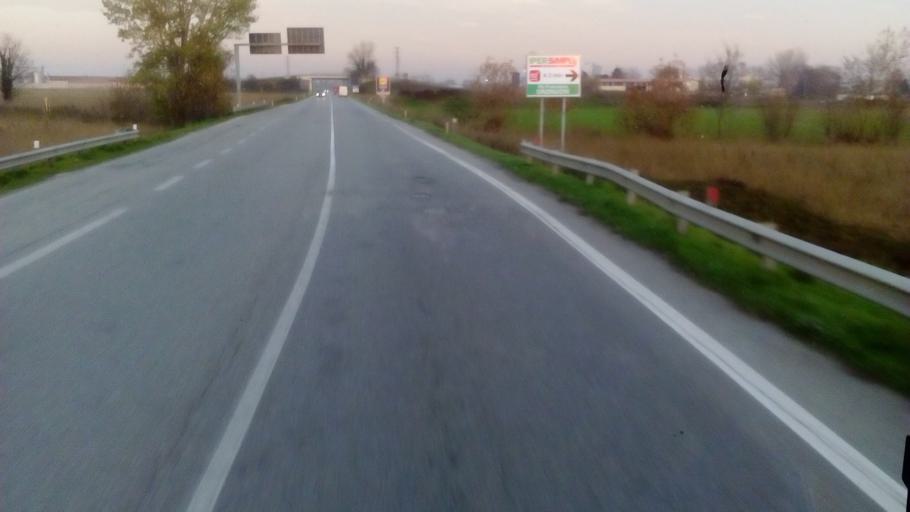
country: IT
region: Lombardy
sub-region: Provincia di Brescia
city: Orzinuovi
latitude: 45.4146
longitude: 9.9288
